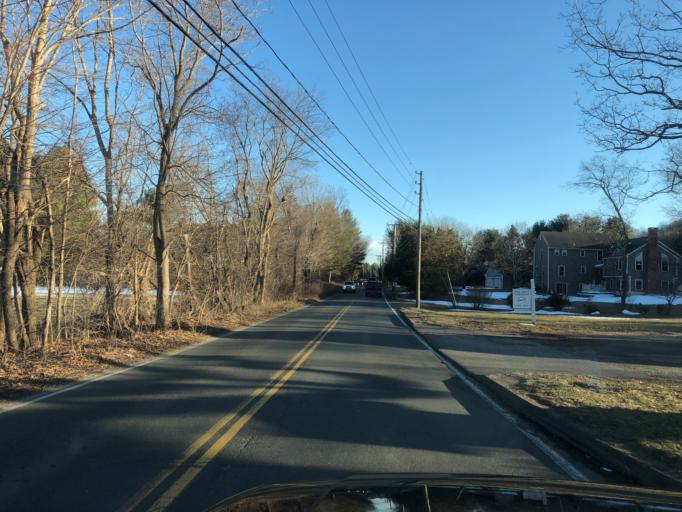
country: US
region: Connecticut
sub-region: Hartford County
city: Farmington
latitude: 41.7690
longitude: -72.8596
